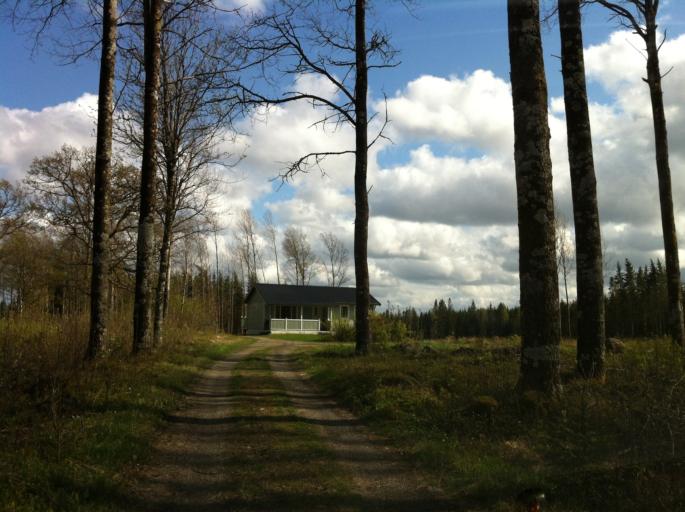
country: SE
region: Vaestra Goetaland
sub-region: Bollebygds Kommun
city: Bollebygd
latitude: 57.7646
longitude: 12.5886
